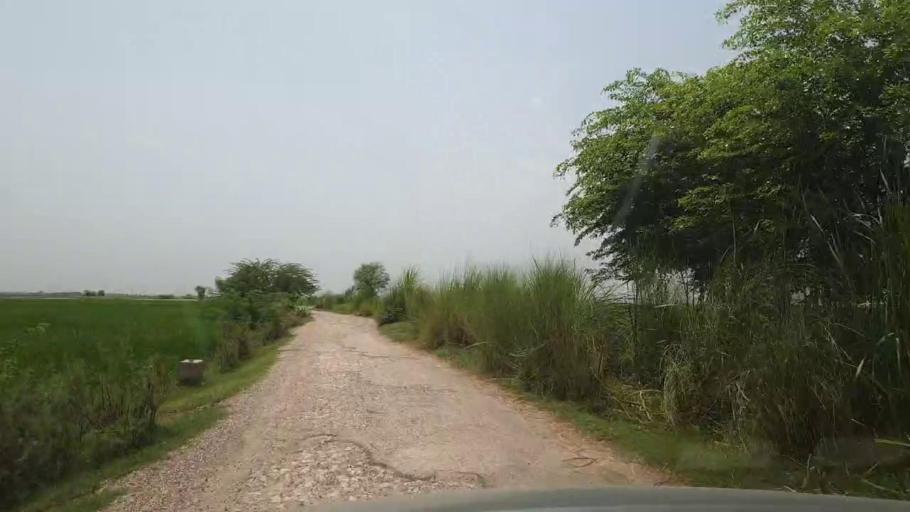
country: PK
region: Sindh
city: Garhi Yasin
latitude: 27.8725
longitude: 68.5009
